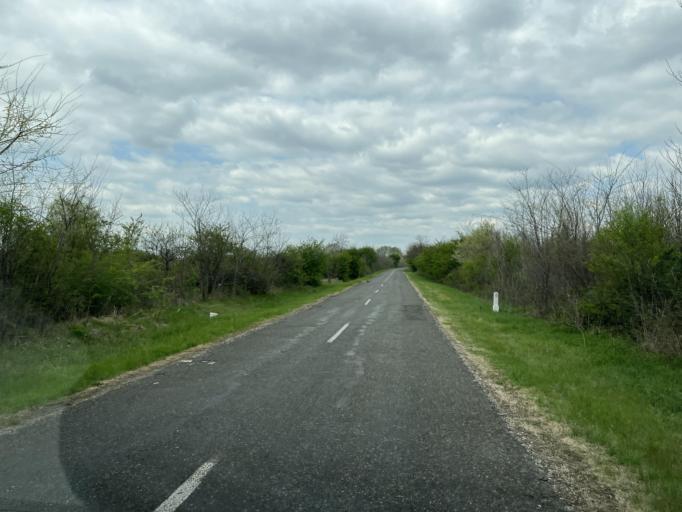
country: HU
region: Pest
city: Dabas
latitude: 47.1321
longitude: 19.3378
